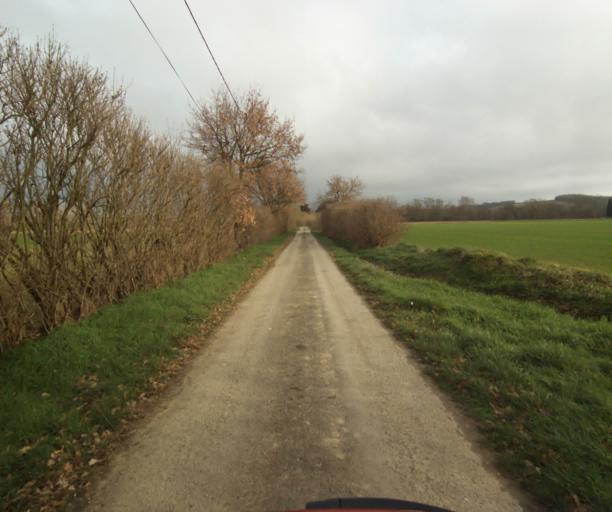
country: FR
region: Languedoc-Roussillon
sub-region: Departement de l'Aude
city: Belpech
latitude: 43.1894
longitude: 1.7320
